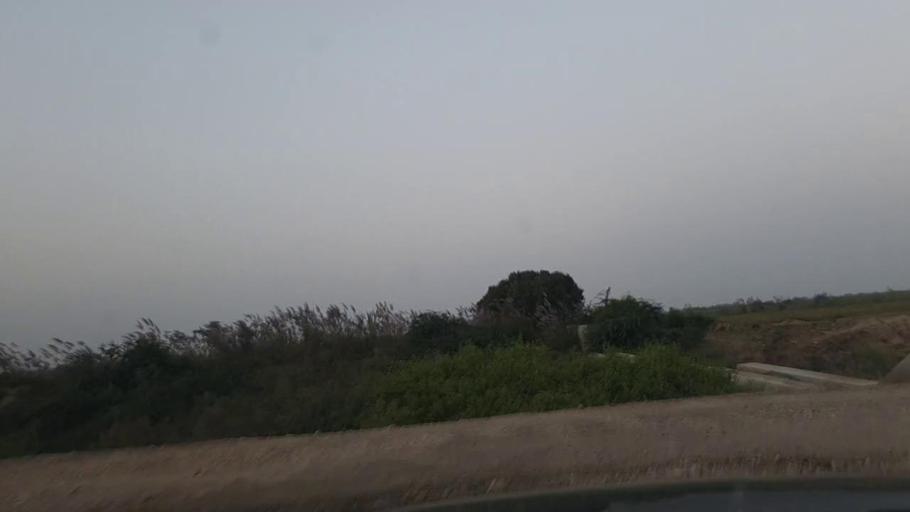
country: PK
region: Sindh
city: Mirpur Sakro
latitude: 24.6348
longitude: 67.7070
